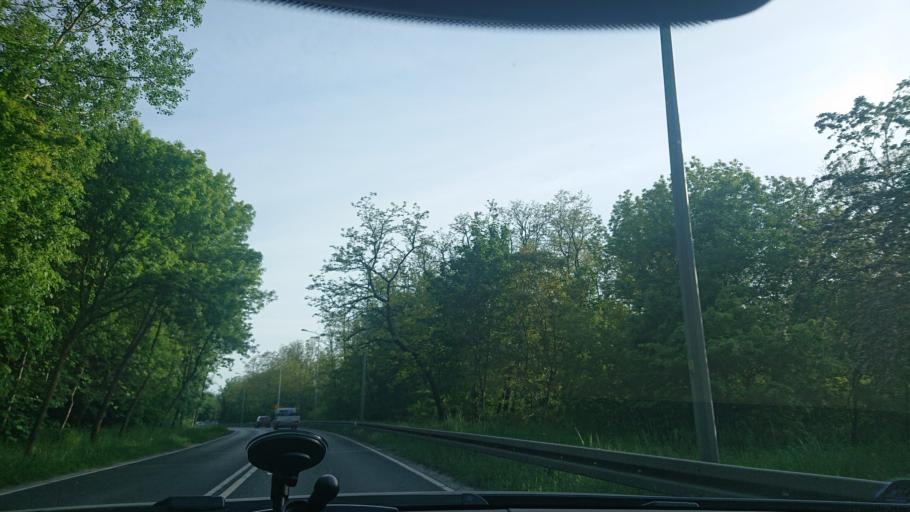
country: PL
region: Greater Poland Voivodeship
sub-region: Powiat gnieznienski
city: Gniezno
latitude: 52.5221
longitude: 17.5838
